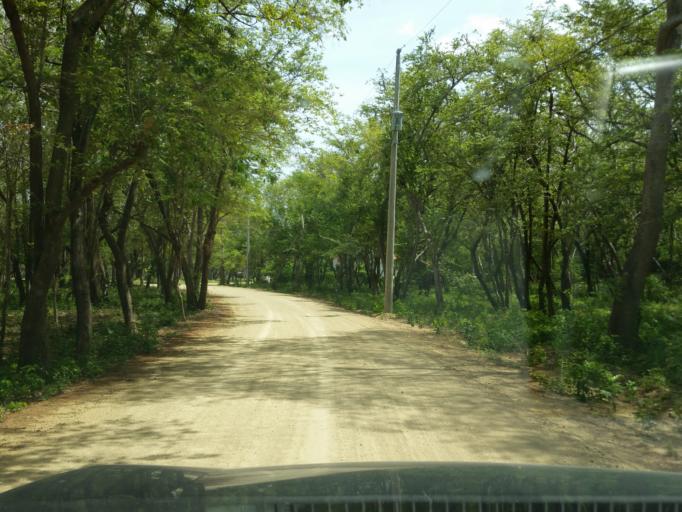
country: NI
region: Rivas
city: Tola
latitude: 11.4104
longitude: -86.0469
